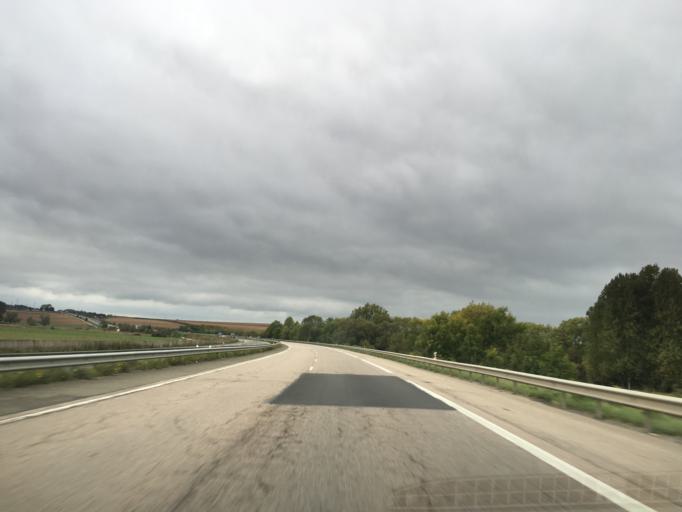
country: FR
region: Lorraine
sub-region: Departement de Meurthe-et-Moselle
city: Foug
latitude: 48.6885
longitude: 5.7062
